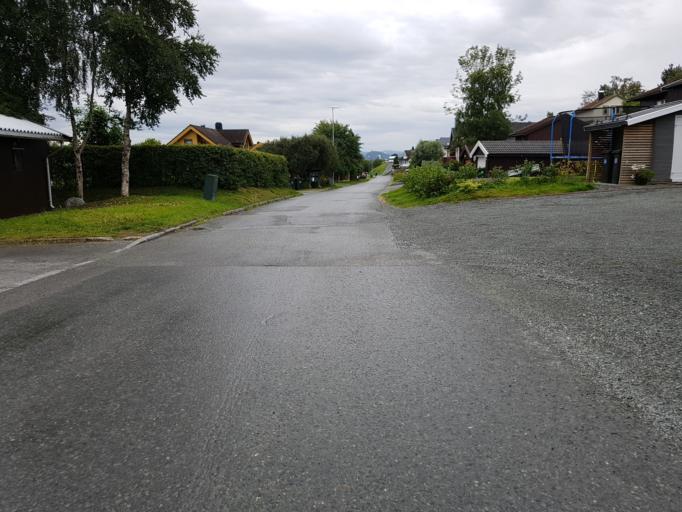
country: NO
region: Sor-Trondelag
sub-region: Trondheim
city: Trondheim
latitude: 63.3879
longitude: 10.3352
